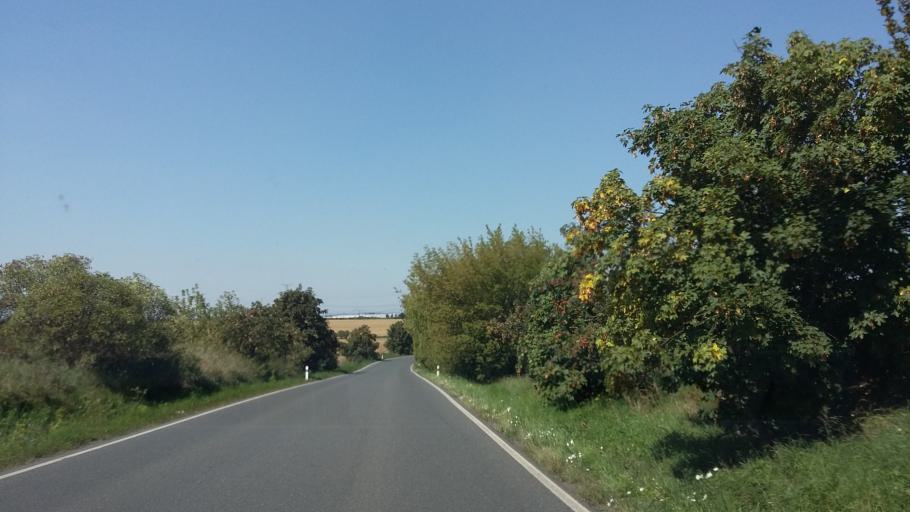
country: CZ
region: Central Bohemia
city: Jirny
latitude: 50.1465
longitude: 14.6902
